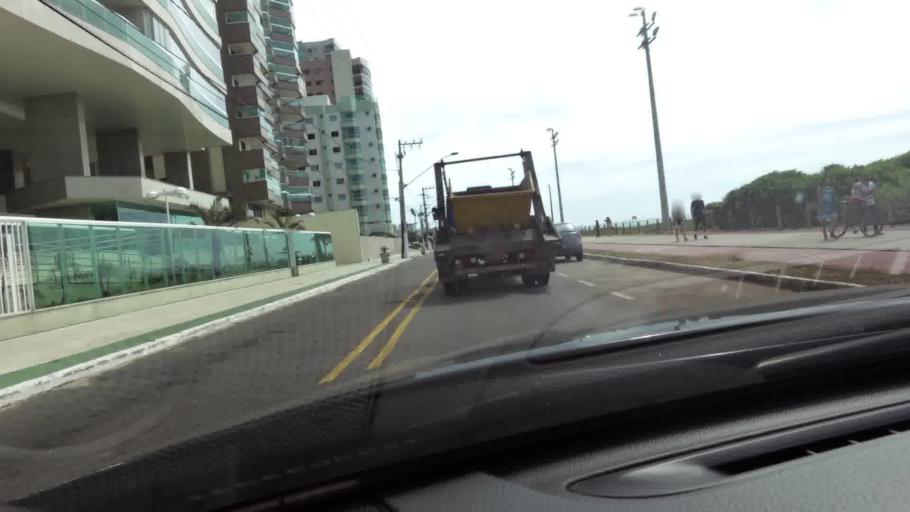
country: BR
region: Espirito Santo
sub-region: Vila Velha
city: Vila Velha
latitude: -20.3778
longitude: -40.3063
